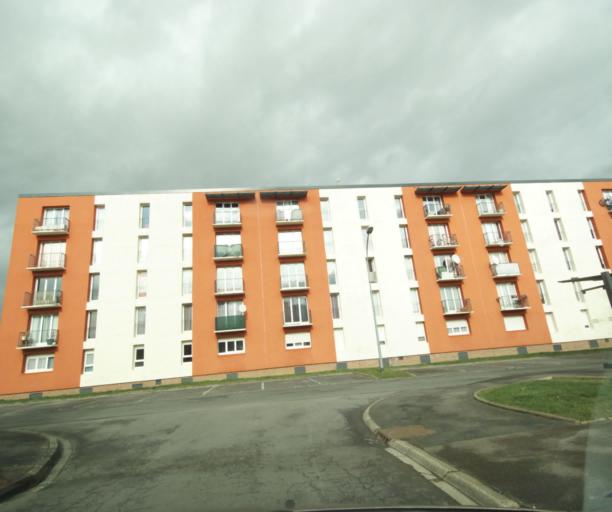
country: FR
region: Picardie
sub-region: Departement de l'Oise
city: Noyon
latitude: 49.5792
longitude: 2.9882
